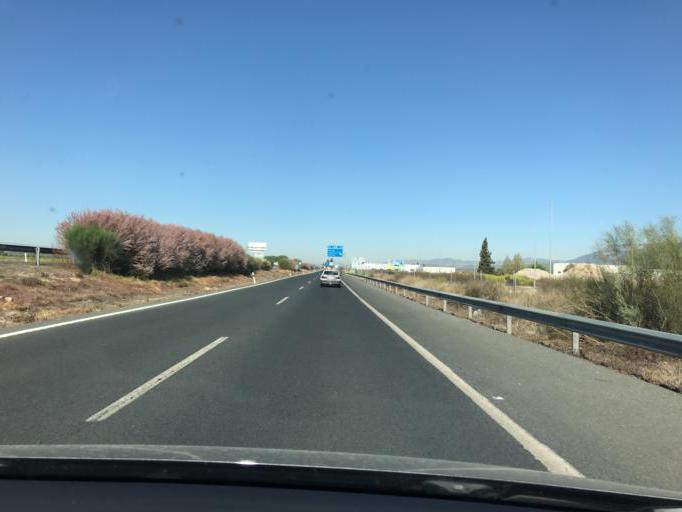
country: ES
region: Andalusia
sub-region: Provincia de Granada
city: Chauchina
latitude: 37.1927
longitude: -3.7910
